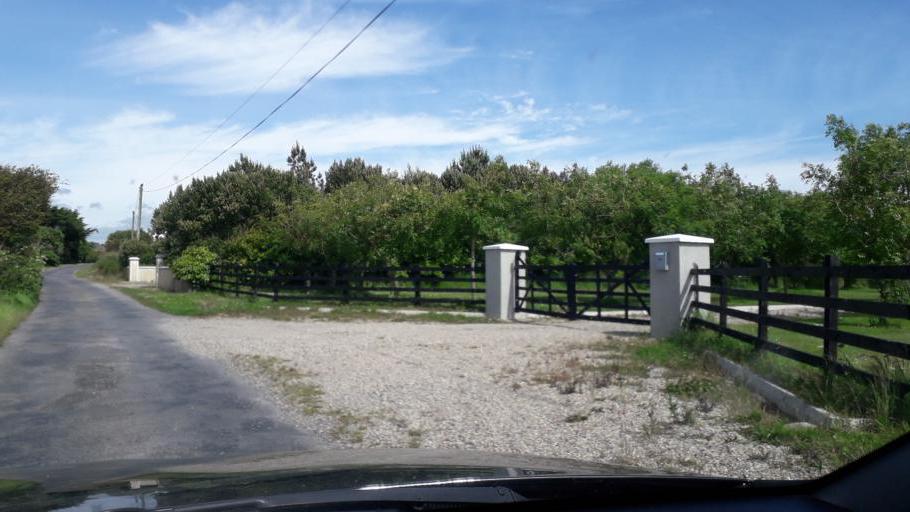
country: IE
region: Leinster
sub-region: Loch Garman
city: Loch Garman
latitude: 52.1900
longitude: -6.5441
